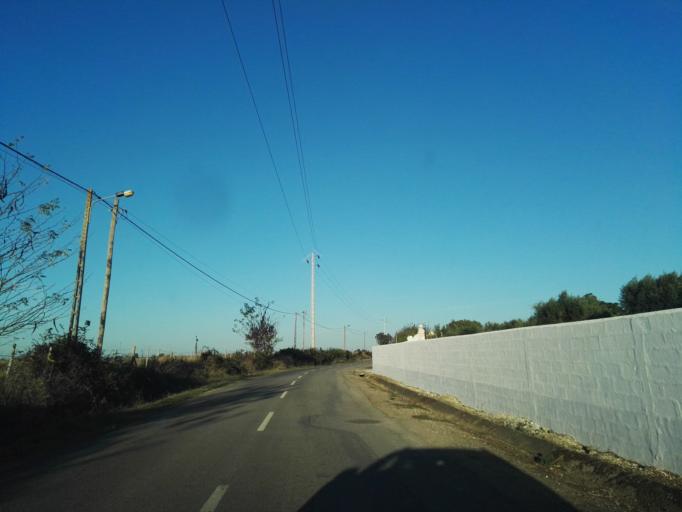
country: PT
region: Santarem
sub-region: Alpiarca
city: Alpiarca
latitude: 39.3455
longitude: -8.5621
